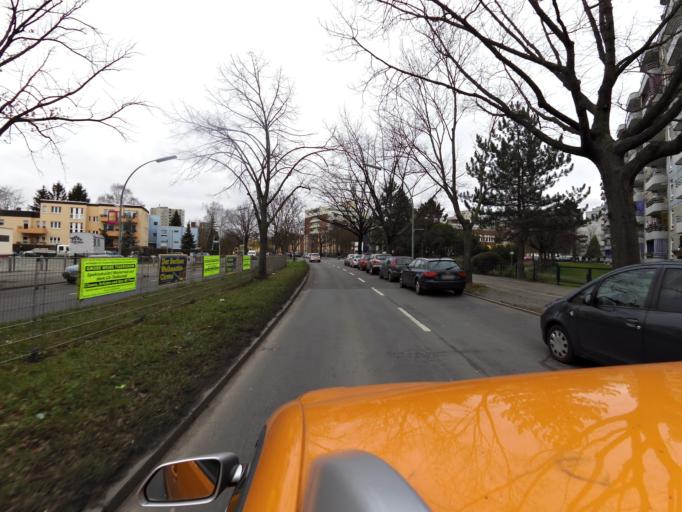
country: DE
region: Berlin
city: Buckow
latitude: 52.4329
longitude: 13.4591
